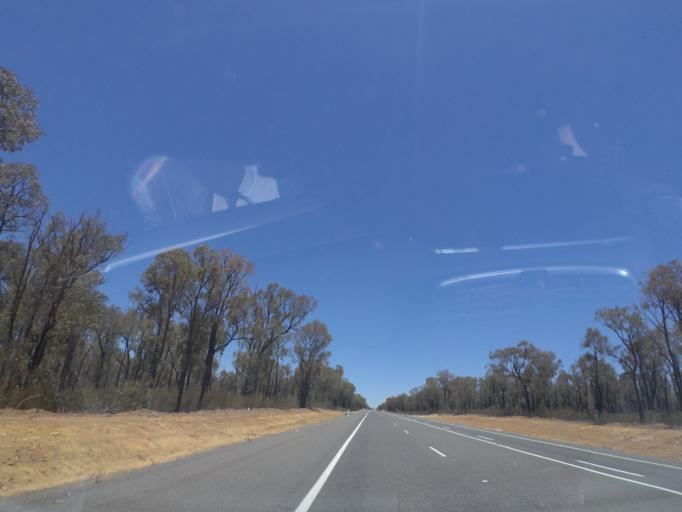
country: AU
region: New South Wales
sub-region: Warrumbungle Shire
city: Coonabarabran
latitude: -30.8963
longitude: 149.4408
